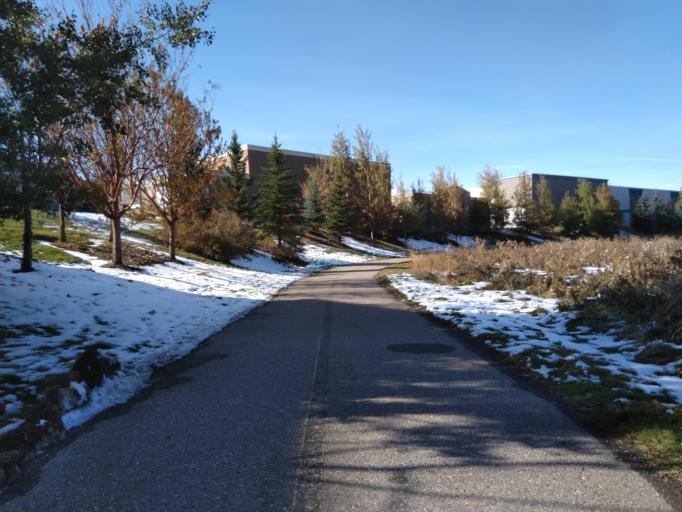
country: CA
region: Alberta
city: Calgary
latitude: 51.1637
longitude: -114.1252
